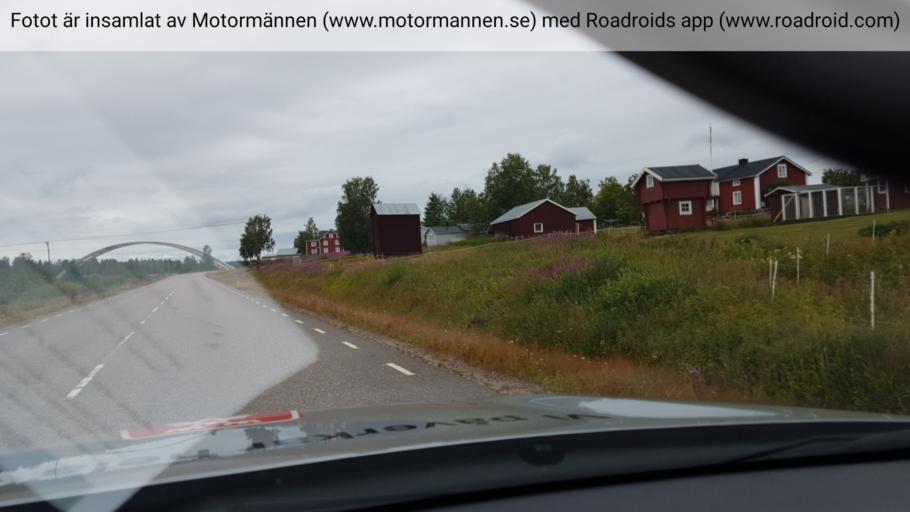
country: SE
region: Norrbotten
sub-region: Pajala Kommun
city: Pajala
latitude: 67.1649
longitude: 22.6199
